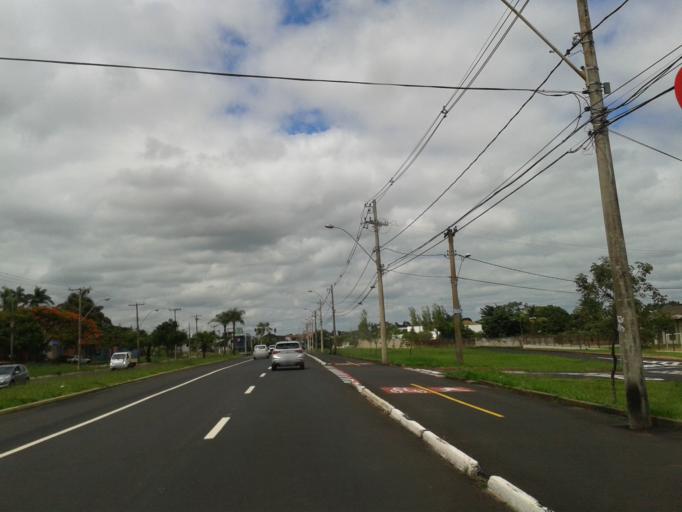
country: BR
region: Minas Gerais
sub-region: Uberaba
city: Uberaba
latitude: -19.7456
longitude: -47.9649
